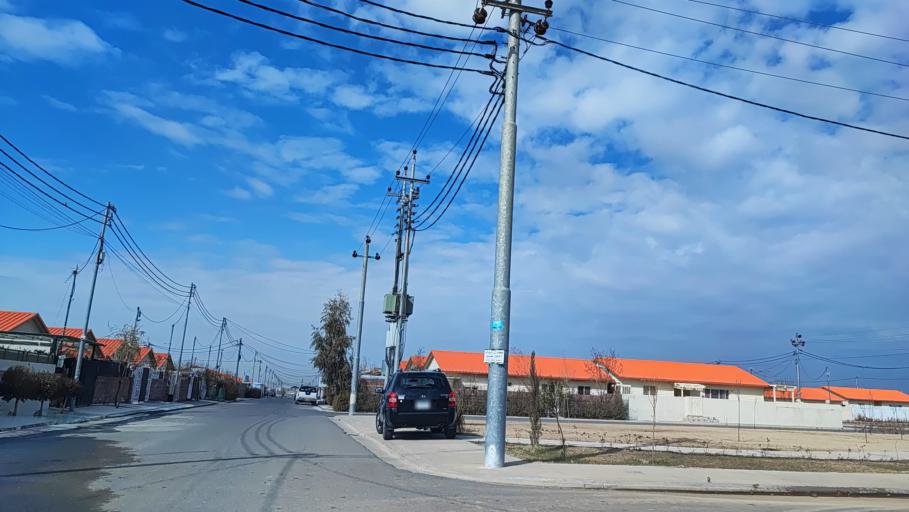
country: IQ
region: Arbil
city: Erbil
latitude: 36.2855
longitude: 44.0679
